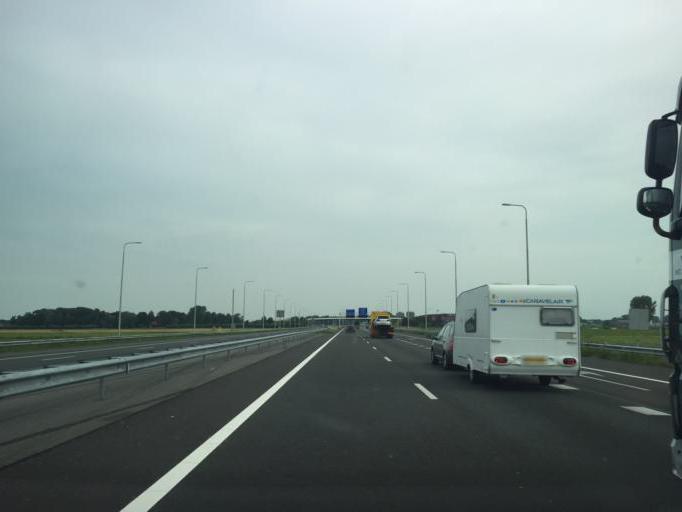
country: NL
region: North Holland
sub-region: Gemeente Alkmaar
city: Alkmaar
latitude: 52.6022
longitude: 4.7303
